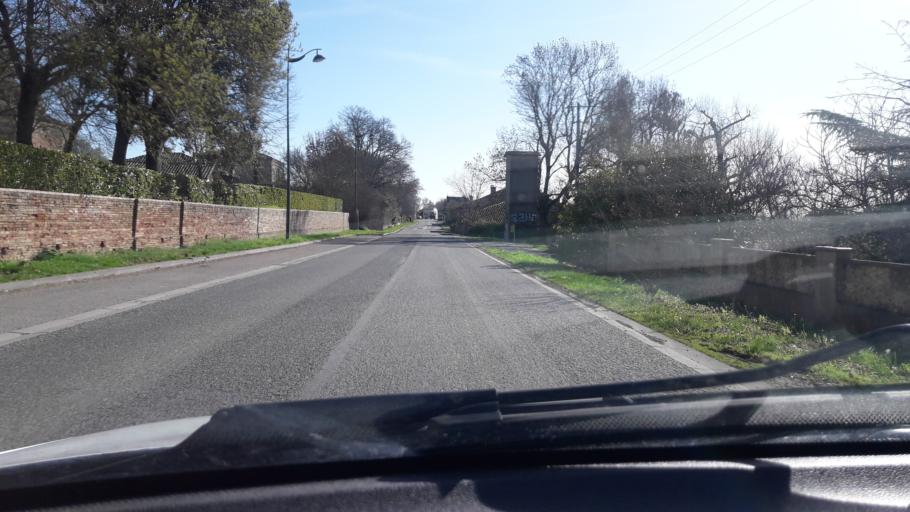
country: FR
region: Midi-Pyrenees
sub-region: Departement du Gers
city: Pujaudran
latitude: 43.6630
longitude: 1.0222
